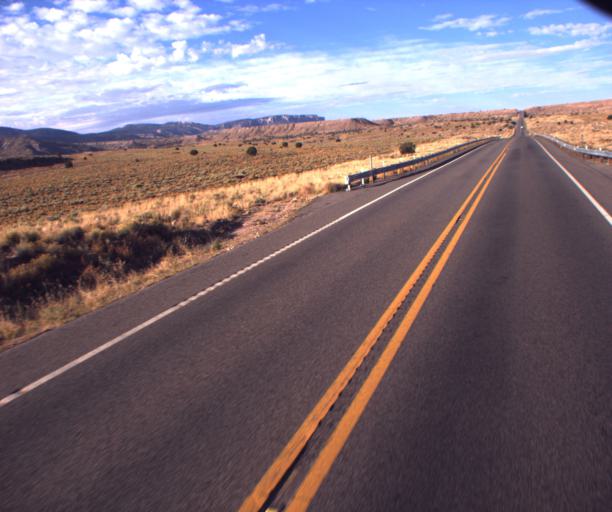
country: US
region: New Mexico
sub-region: San Juan County
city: Shiprock
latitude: 36.9344
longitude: -109.1327
